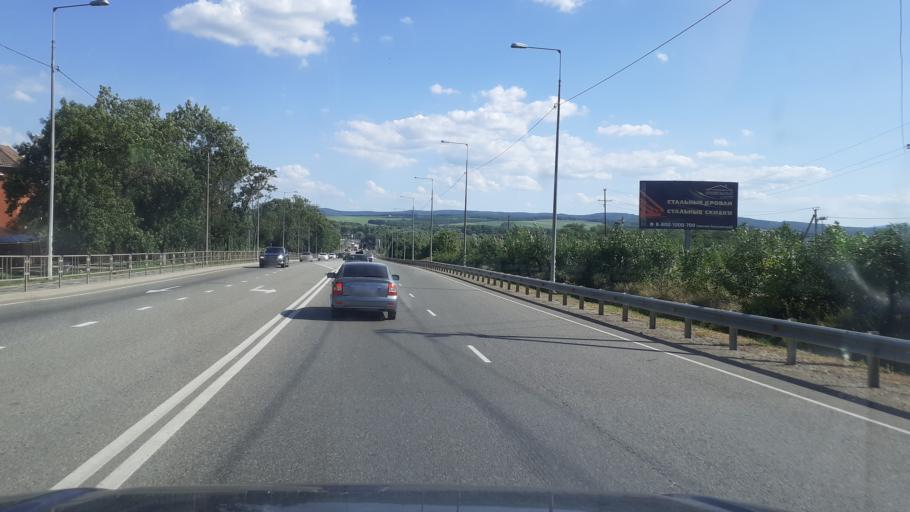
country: RU
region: Krasnodarskiy
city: Severskaya
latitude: 44.8405
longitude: 38.6591
